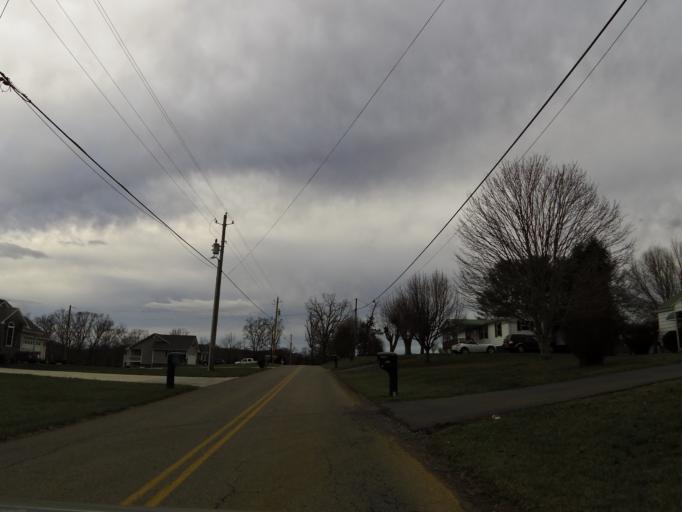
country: US
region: Tennessee
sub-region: Greene County
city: Tusculum
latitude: 36.2007
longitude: -82.7410
